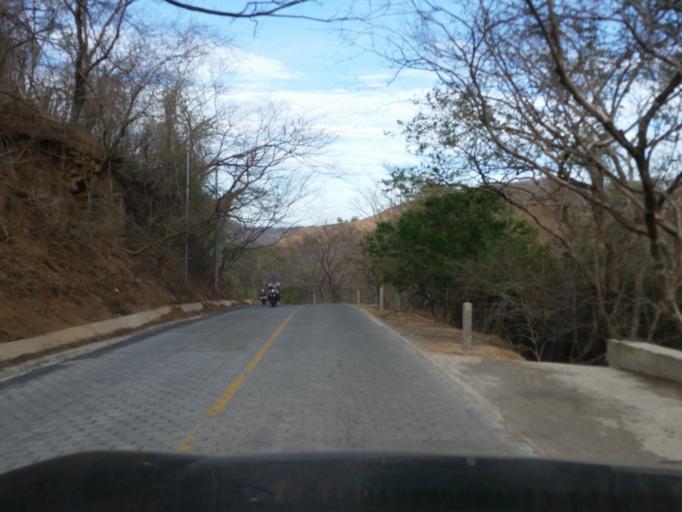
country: NI
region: Rivas
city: Tola
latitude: 11.3916
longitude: -85.9785
